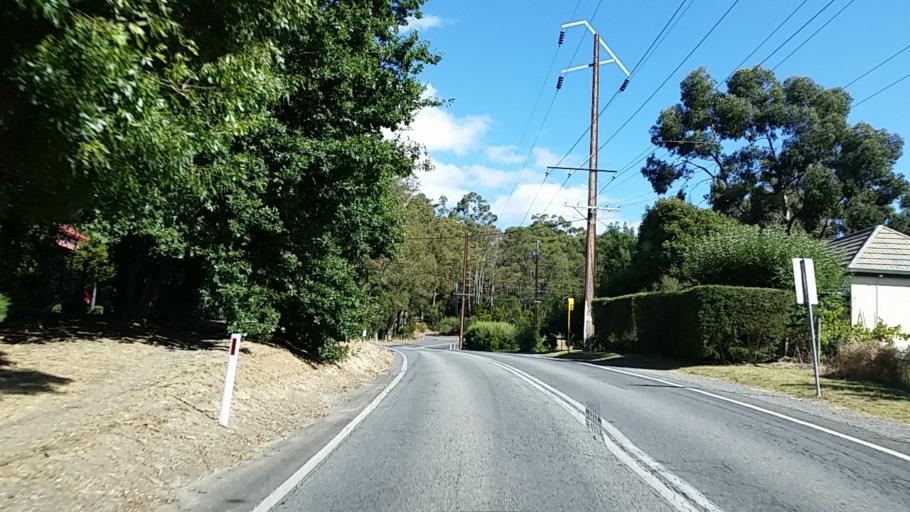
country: AU
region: South Australia
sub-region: Adelaide Hills
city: Bridgewater
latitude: -34.9846
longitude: 138.7262
